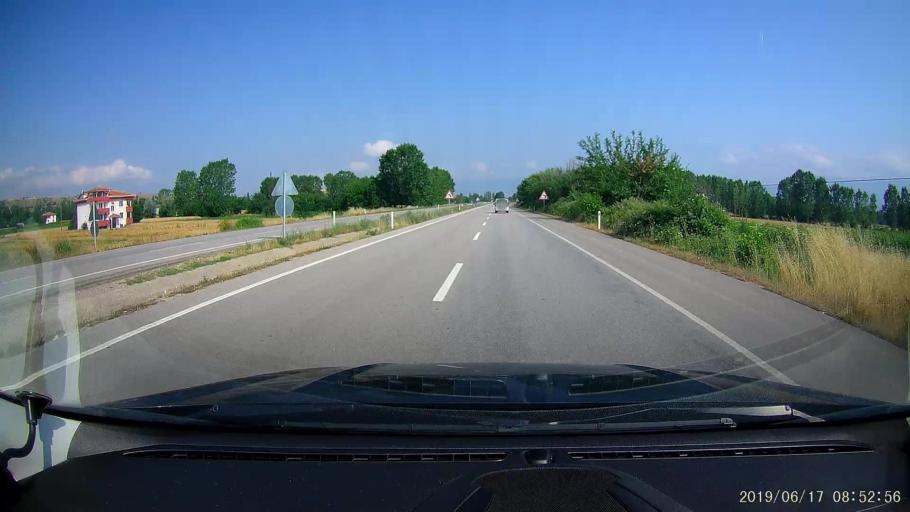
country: TR
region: Tokat
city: Erbaa
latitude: 40.7041
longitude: 36.4890
